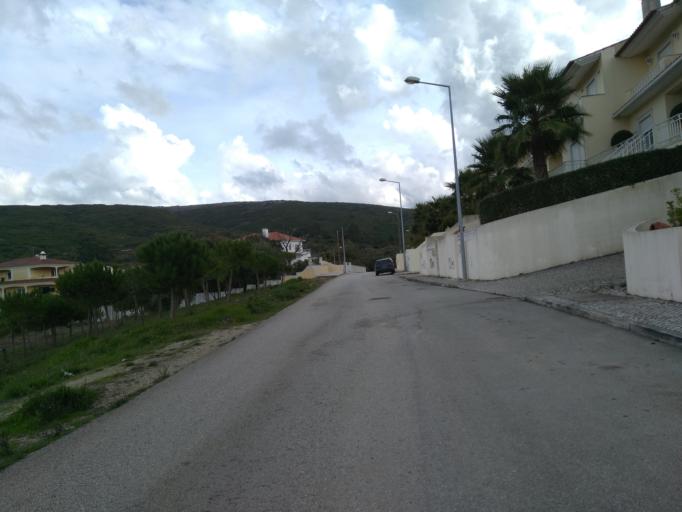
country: PT
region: Leiria
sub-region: Porto de Mos
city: Porto de Mos
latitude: 39.5977
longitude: -8.8094
